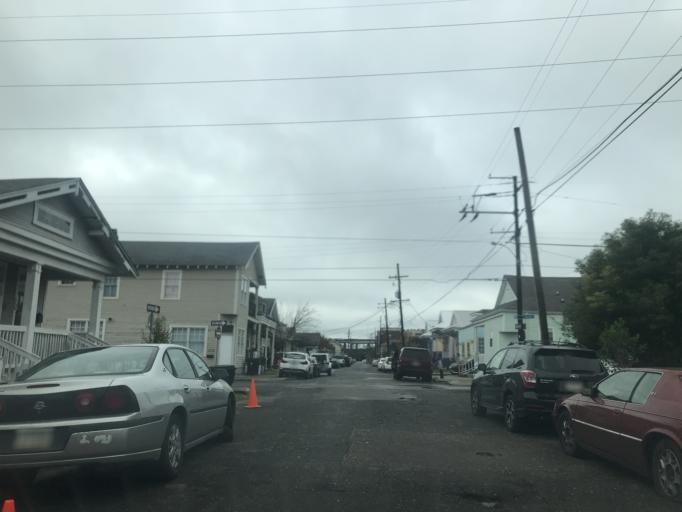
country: US
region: Louisiana
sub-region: Orleans Parish
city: New Orleans
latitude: 29.9730
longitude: -90.1062
